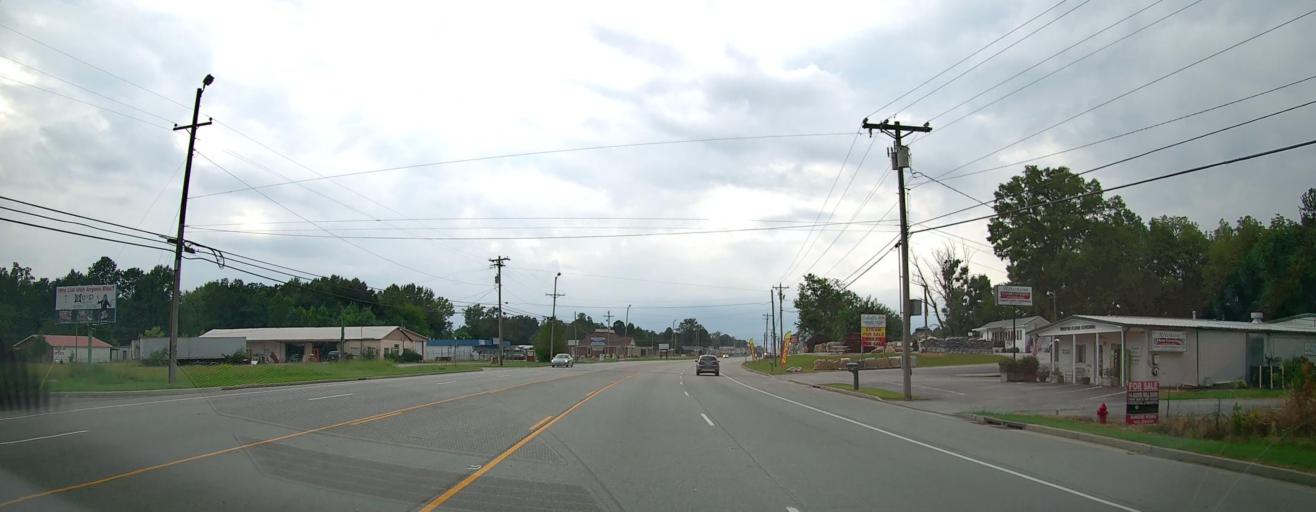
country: US
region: Tennessee
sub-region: Coffee County
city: Manchester
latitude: 35.4627
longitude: -86.0653
